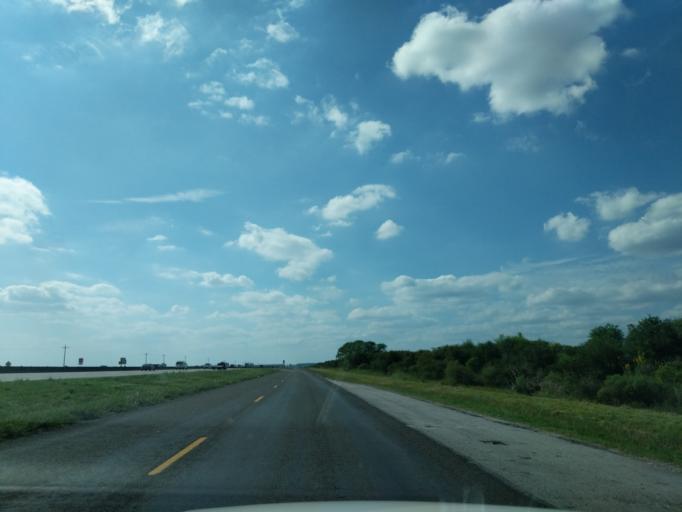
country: US
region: Texas
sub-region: Chambers County
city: Anahuac
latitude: 29.8350
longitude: -94.5422
